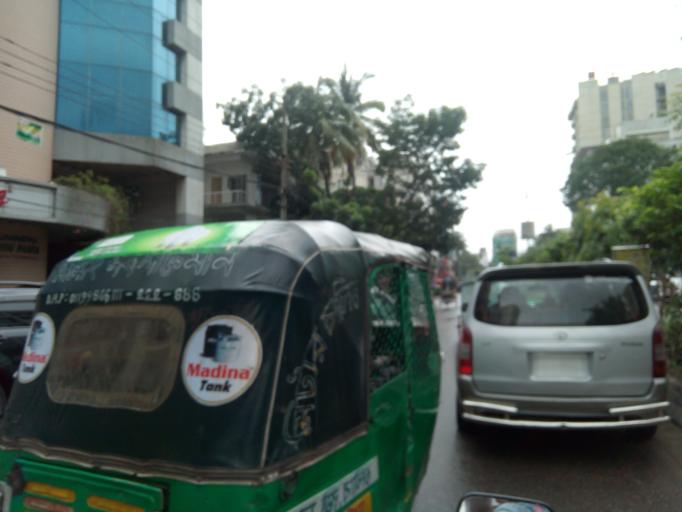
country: BD
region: Dhaka
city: Azimpur
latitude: 23.7534
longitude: 90.3706
